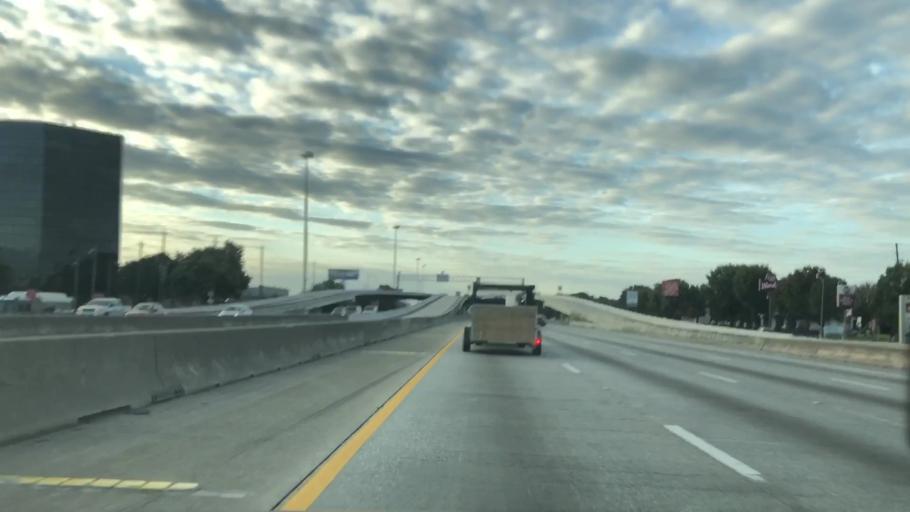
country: US
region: Texas
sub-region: Harris County
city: Aldine
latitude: 29.9223
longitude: -95.4124
